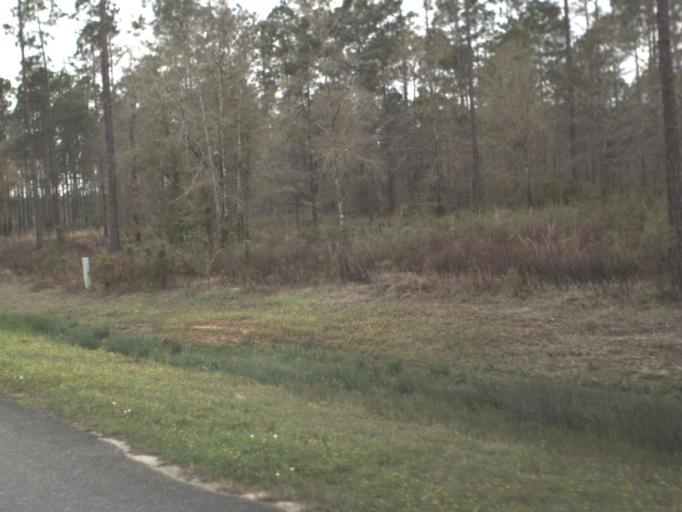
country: US
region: Florida
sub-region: Calhoun County
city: Blountstown
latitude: 30.4310
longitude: -85.1902
